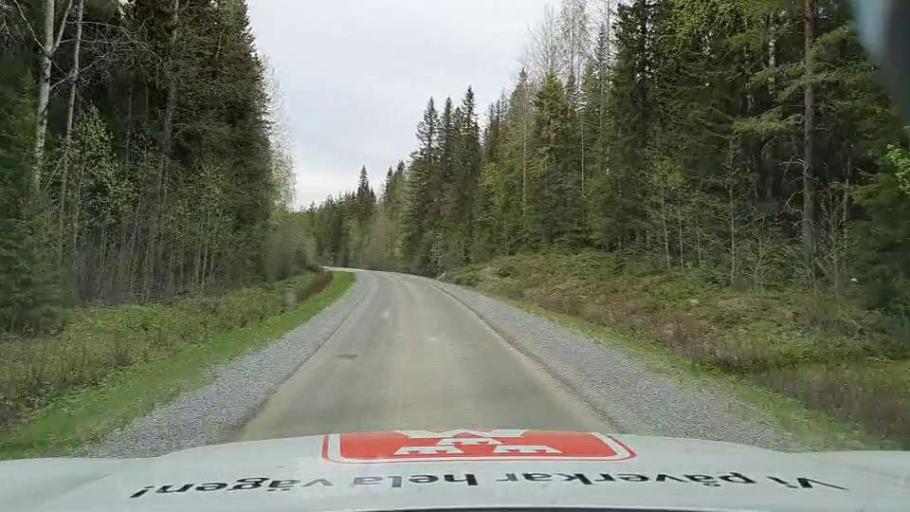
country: SE
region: Jaemtland
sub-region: OEstersunds Kommun
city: Brunflo
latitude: 62.6394
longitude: 14.9345
